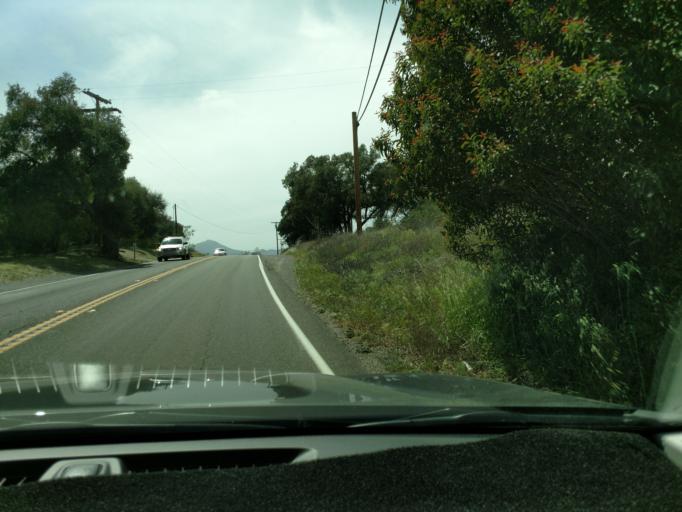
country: US
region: California
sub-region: San Diego County
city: Ramona
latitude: 33.0471
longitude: -116.8253
